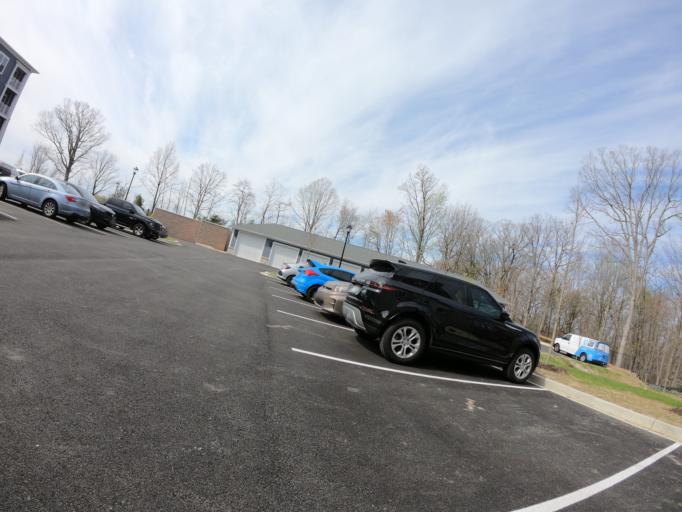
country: US
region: Maryland
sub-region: Howard County
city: Ilchester
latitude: 39.2067
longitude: -76.7871
